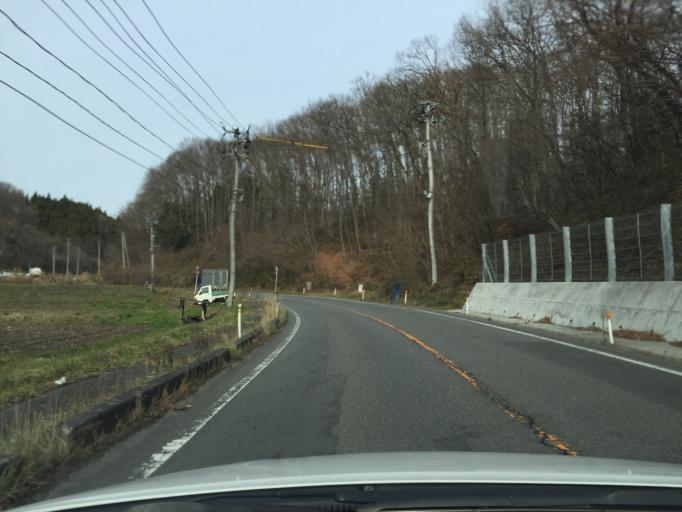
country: JP
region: Fukushima
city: Funehikimachi-funehiki
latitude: 37.2618
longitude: 140.6312
